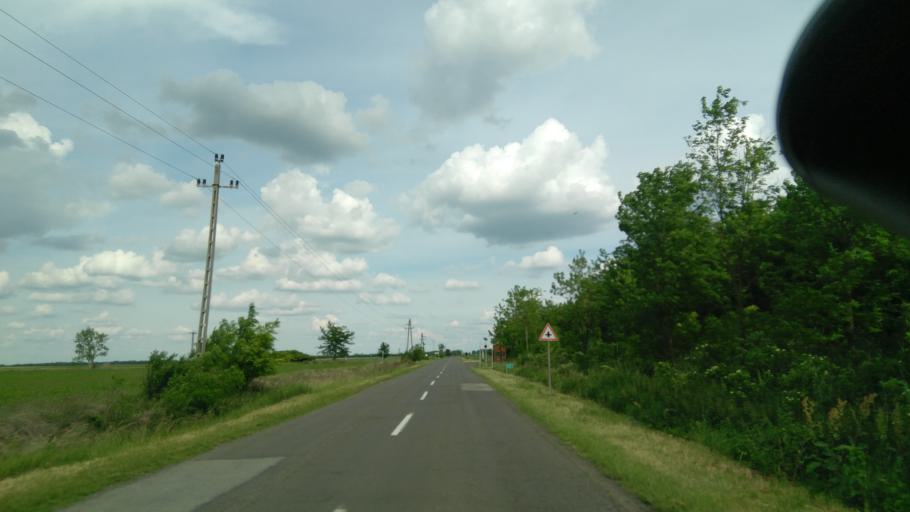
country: RO
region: Arad
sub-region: Comuna Peregu Mare
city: Peregu Mic
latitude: 46.3001
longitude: 20.9349
